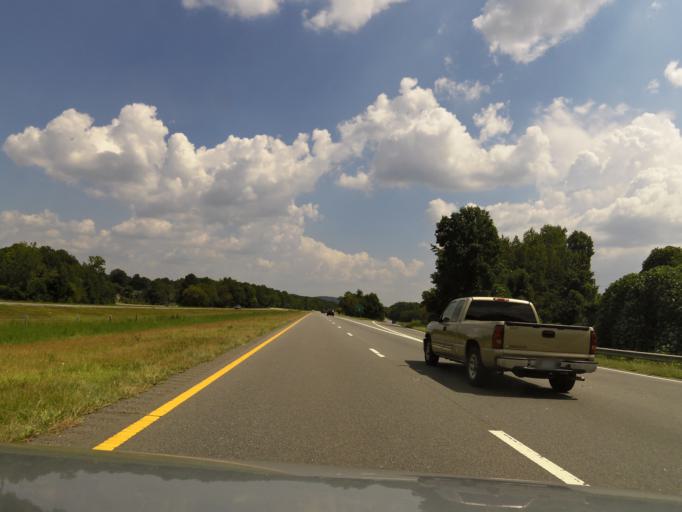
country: US
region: North Carolina
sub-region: Cleveland County
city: Kings Mountain
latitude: 35.2486
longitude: -81.3336
